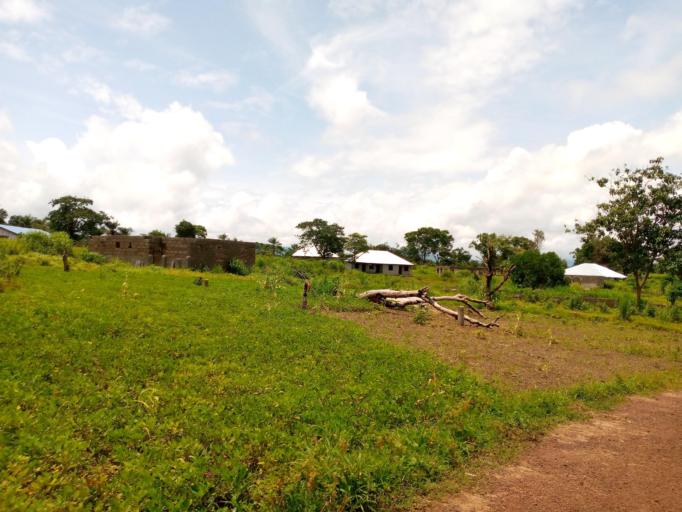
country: SL
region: Northern Province
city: Magburaka
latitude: 8.7249
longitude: -11.9249
